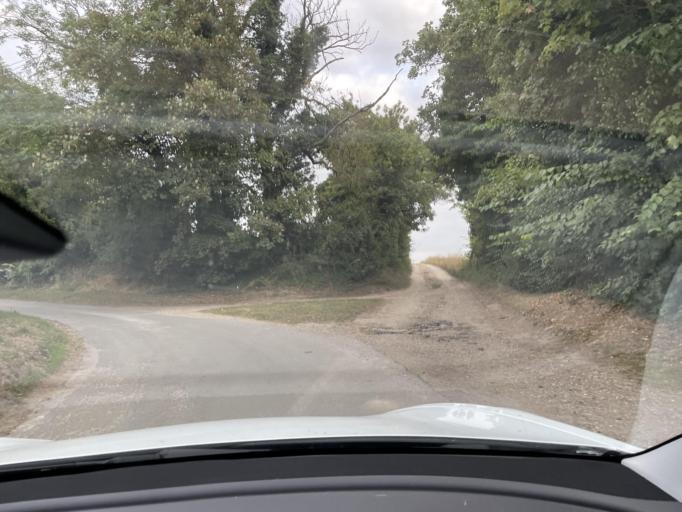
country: GB
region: England
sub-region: Cambridgeshire
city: Harston
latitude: 52.0945
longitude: 0.0967
